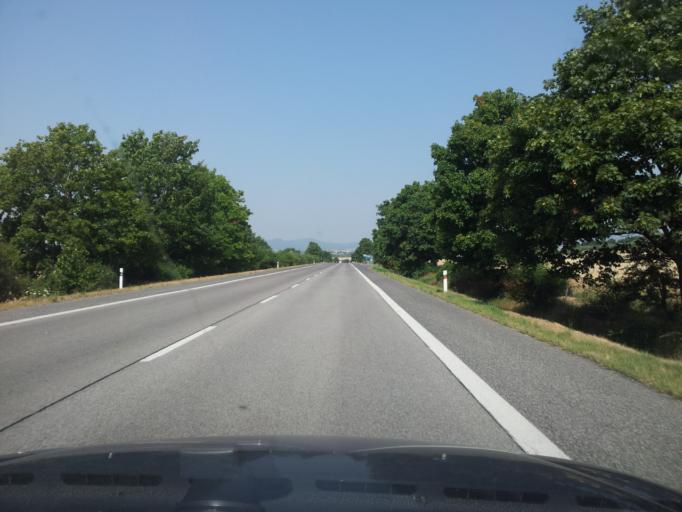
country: SK
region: Nitriansky
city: Zlate Moravce
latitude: 48.3616
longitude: 18.4563
